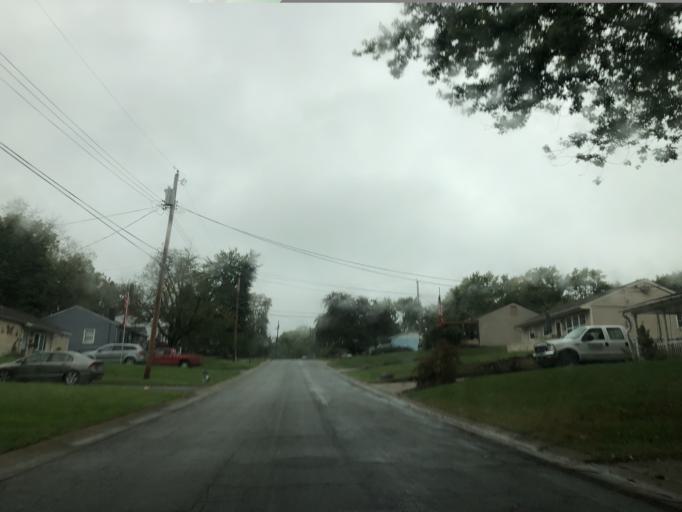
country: US
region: Ohio
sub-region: Hamilton County
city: Loveland
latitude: 39.2658
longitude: -84.2715
